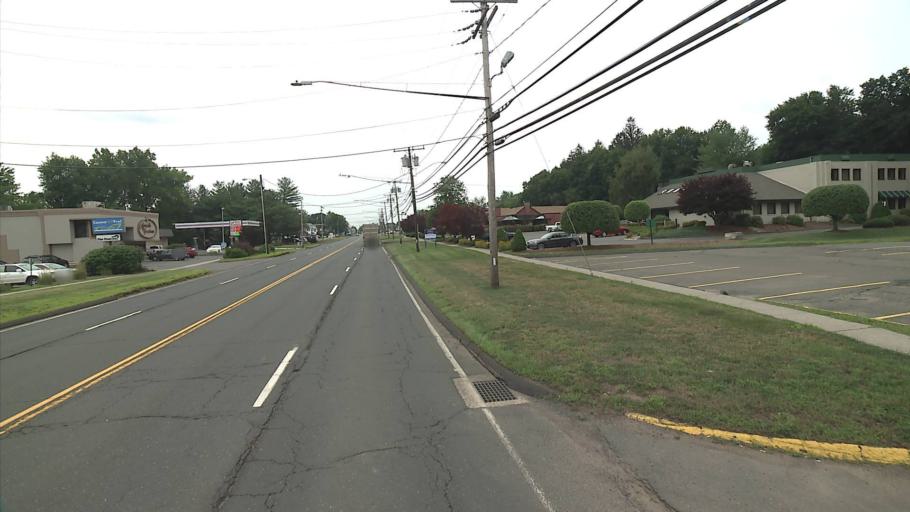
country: US
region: Connecticut
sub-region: Hartford County
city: Wethersfield
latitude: 41.6690
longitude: -72.6424
